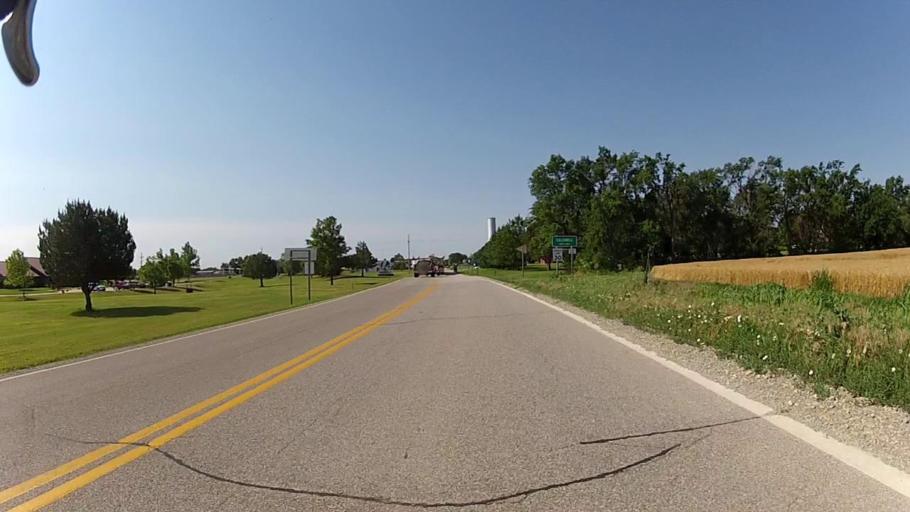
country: US
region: Kansas
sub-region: Sumner County
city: Caldwell
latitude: 37.0430
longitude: -97.6069
